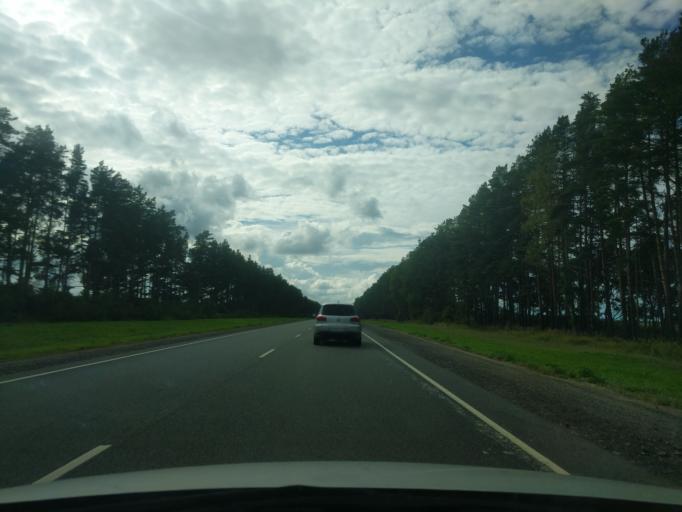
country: RU
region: Jaroslavl
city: Levashevo
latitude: 57.6431
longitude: 40.5001
